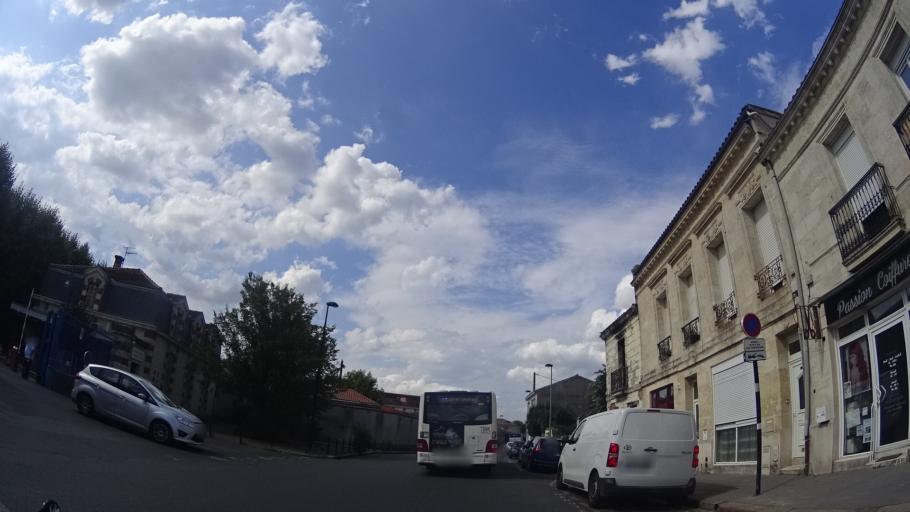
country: FR
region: Aquitaine
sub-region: Departement de la Gironde
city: Begles
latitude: 44.8188
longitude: -0.5662
